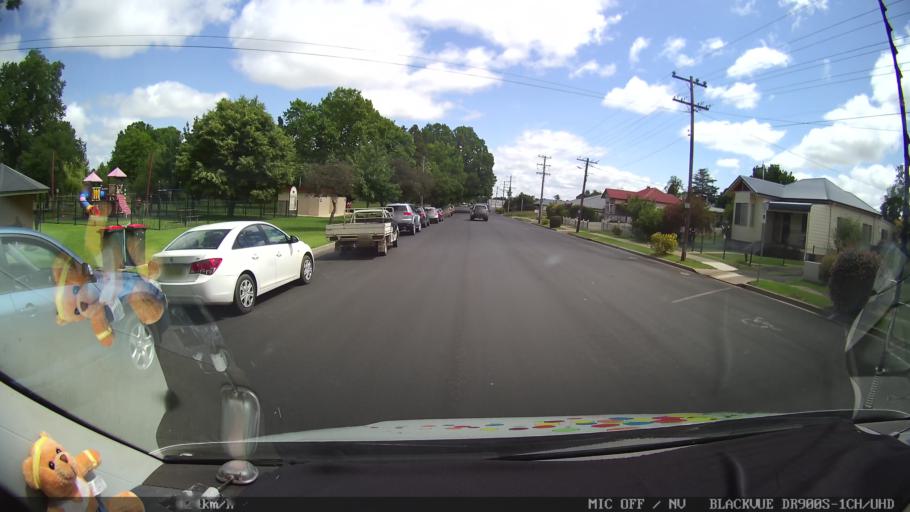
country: AU
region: New South Wales
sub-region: Glen Innes Severn
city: Glen Innes
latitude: -29.7384
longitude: 151.7339
